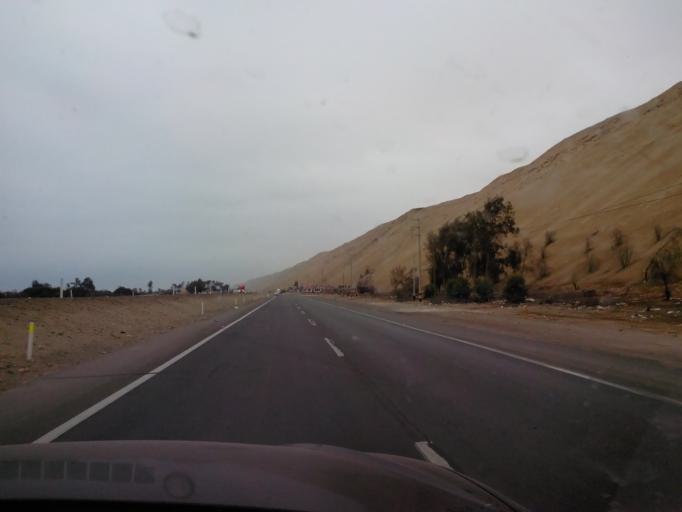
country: PE
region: Ica
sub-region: Provincia de Chincha
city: San Pedro
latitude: -13.3721
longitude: -76.2100
